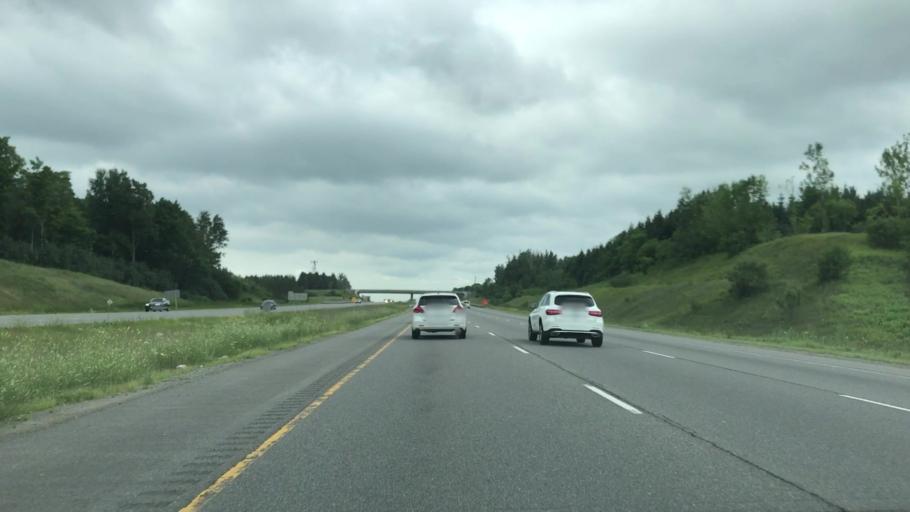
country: CA
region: Ontario
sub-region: York
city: Richmond Hill
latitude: 43.9632
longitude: -79.3930
